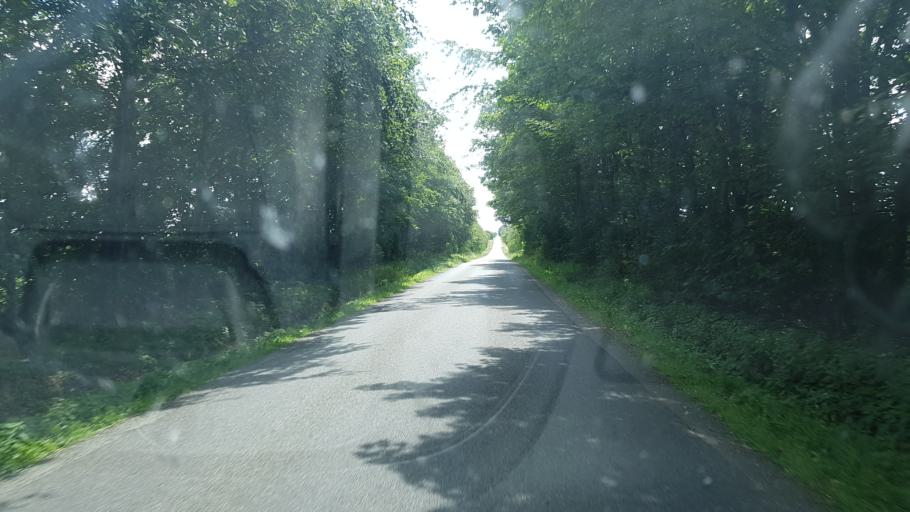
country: DK
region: South Denmark
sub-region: Vejen Kommune
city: Brorup
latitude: 55.4667
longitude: 8.9689
